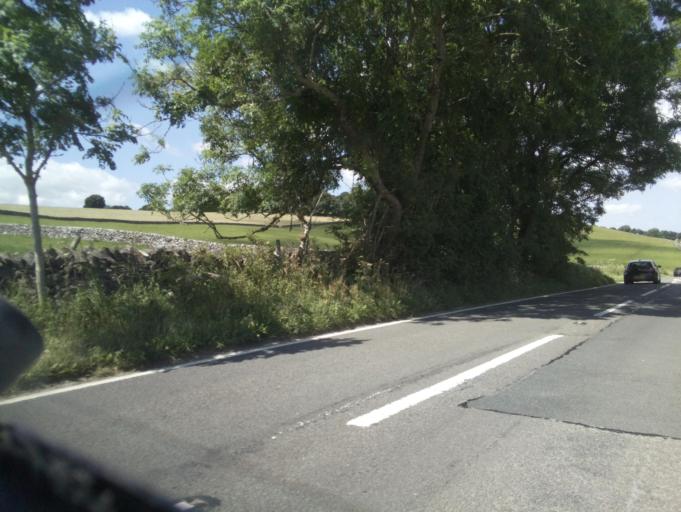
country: GB
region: England
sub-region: Derbyshire
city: Ashbourne
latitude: 53.0761
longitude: -1.7570
